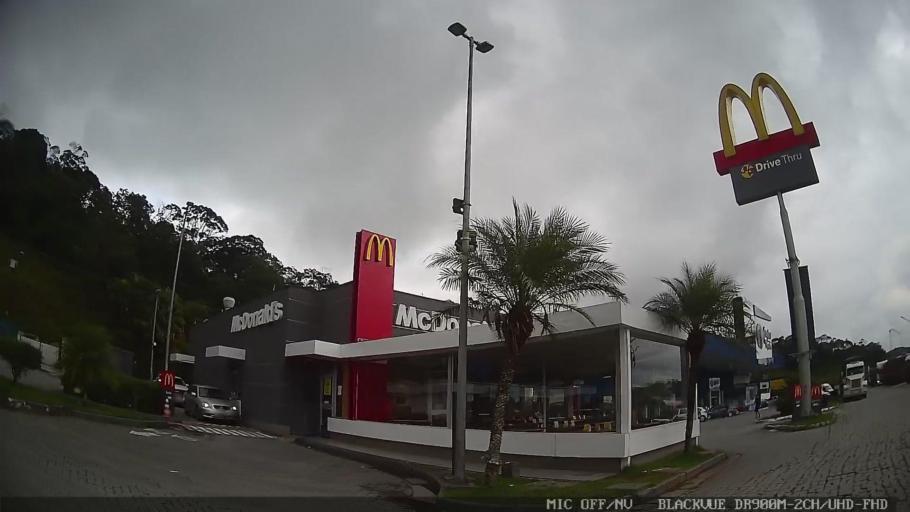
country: BR
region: Sao Paulo
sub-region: Sao Bernardo Do Campo
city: Sao Bernardo do Campo
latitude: -23.8387
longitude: -46.5751
